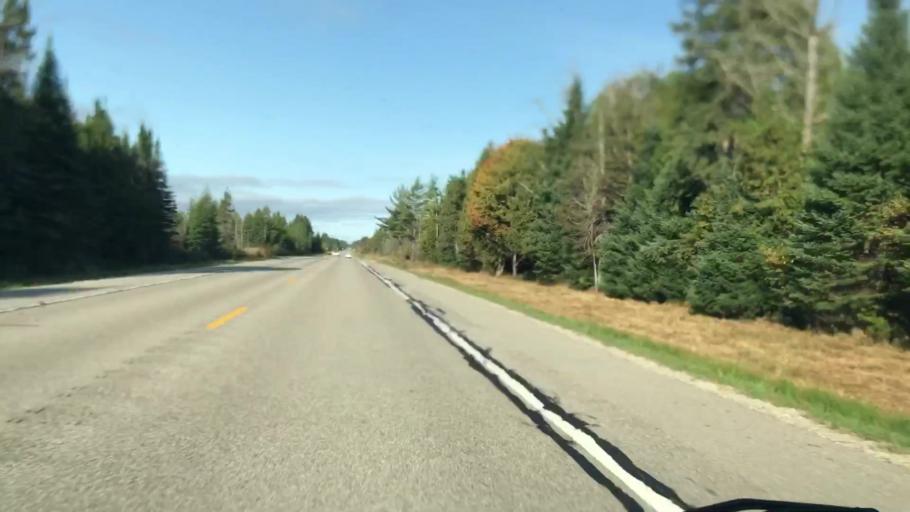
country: US
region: Michigan
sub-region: Luce County
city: Newberry
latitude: 46.3037
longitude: -85.3109
